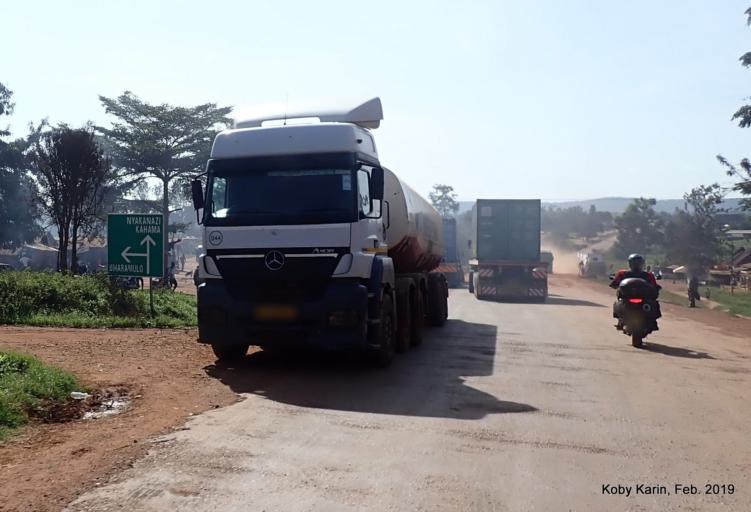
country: TZ
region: Kagera
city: Biharamulo
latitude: -2.9086
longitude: 31.1987
